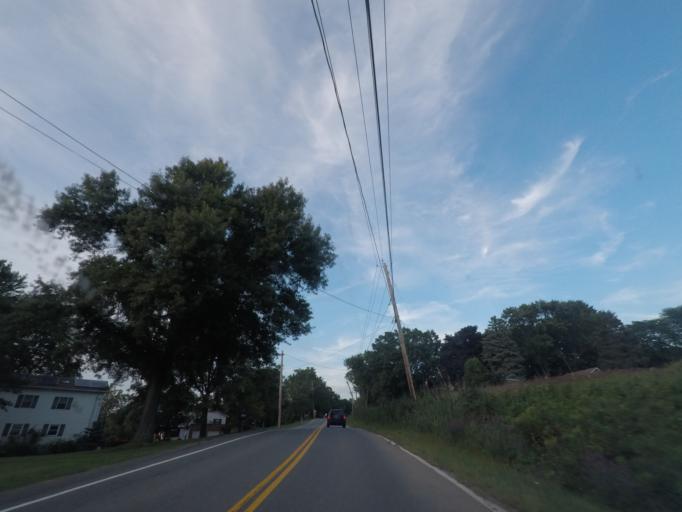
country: US
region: New York
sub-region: Schenectady County
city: Niskayuna
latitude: 42.7790
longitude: -73.7907
